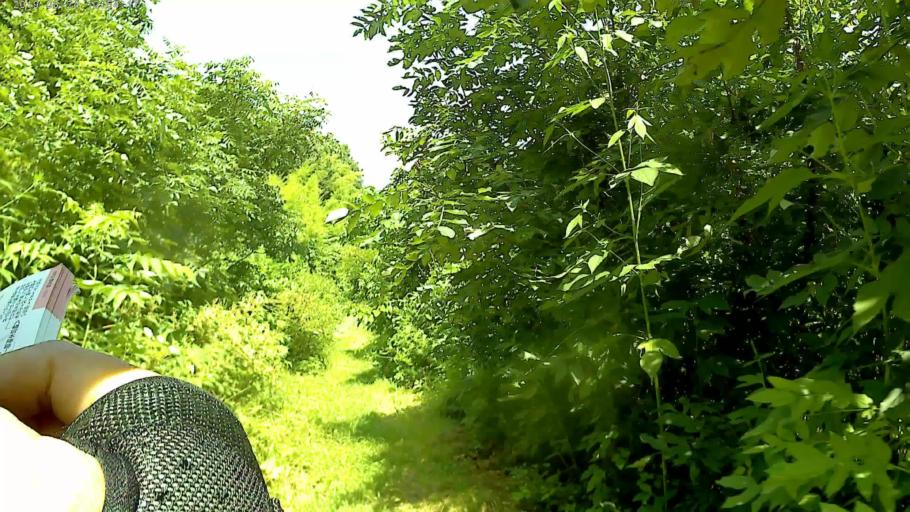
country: JP
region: Nagano
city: Komoro
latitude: 36.2665
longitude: 138.3745
